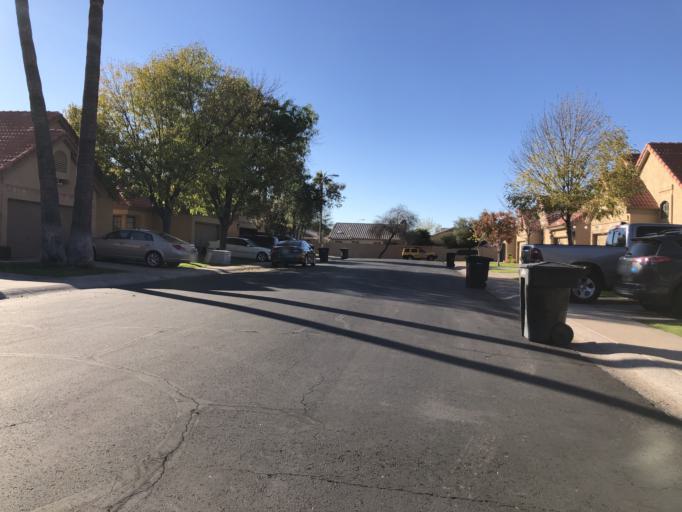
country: US
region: Arizona
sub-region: Maricopa County
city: Guadalupe
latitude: 33.3195
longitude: -111.9230
